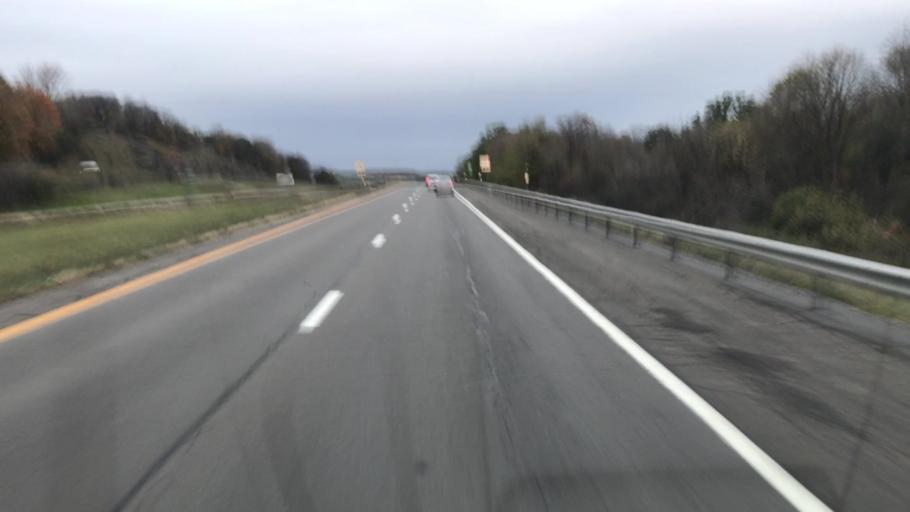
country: US
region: New York
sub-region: Onondaga County
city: Camillus
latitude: 43.0370
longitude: -76.3204
